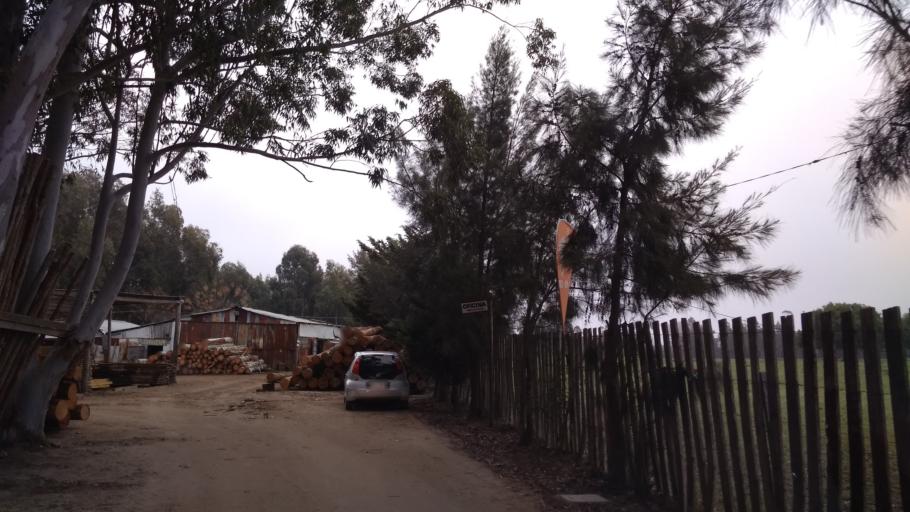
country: UY
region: Florida
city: Florida
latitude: -34.0793
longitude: -56.2024
